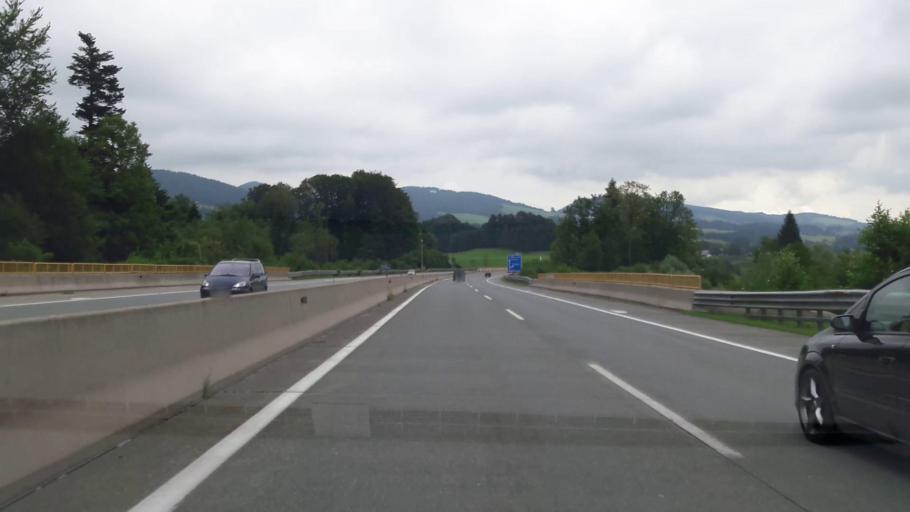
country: AT
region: Salzburg
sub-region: Politischer Bezirk Salzburg-Umgebung
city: Plainfeld
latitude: 47.8537
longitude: 13.1935
